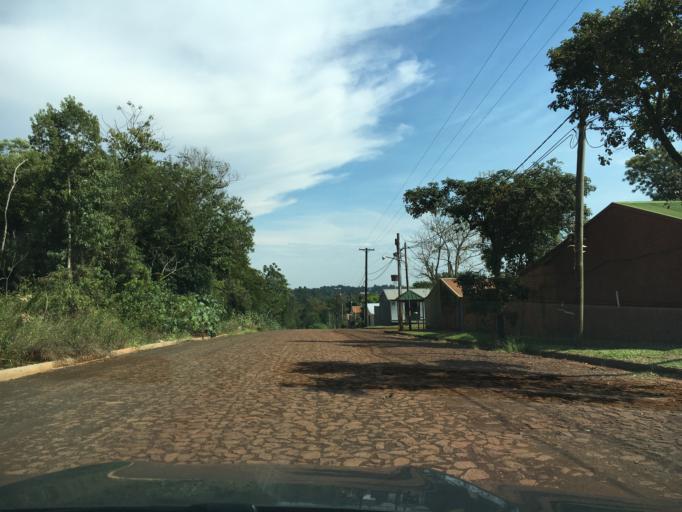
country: AR
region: Misiones
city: Puerto Rico
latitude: -26.8047
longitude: -55.0056
